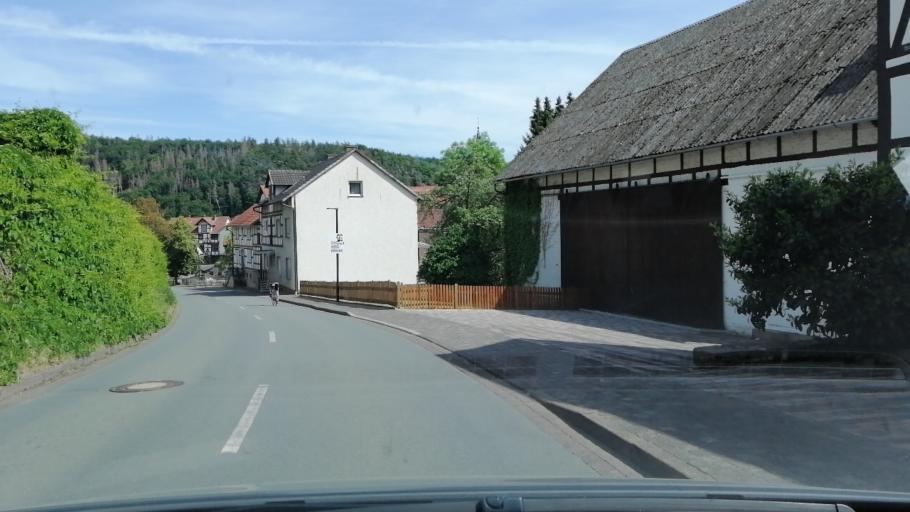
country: DE
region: Hesse
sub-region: Regierungsbezirk Kassel
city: Waldeck
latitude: 51.1723
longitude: 9.0496
